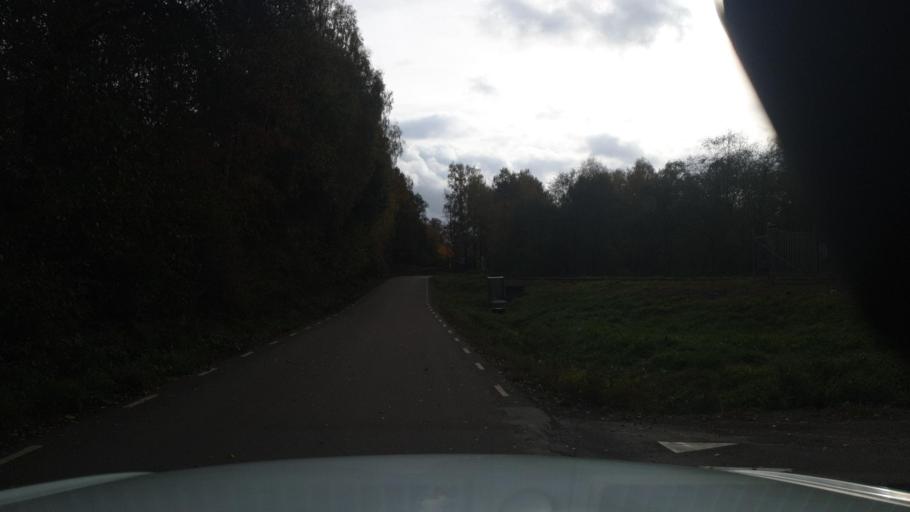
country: SE
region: Vaermland
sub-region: Sunne Kommun
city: Sunne
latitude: 59.7969
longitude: 13.1243
